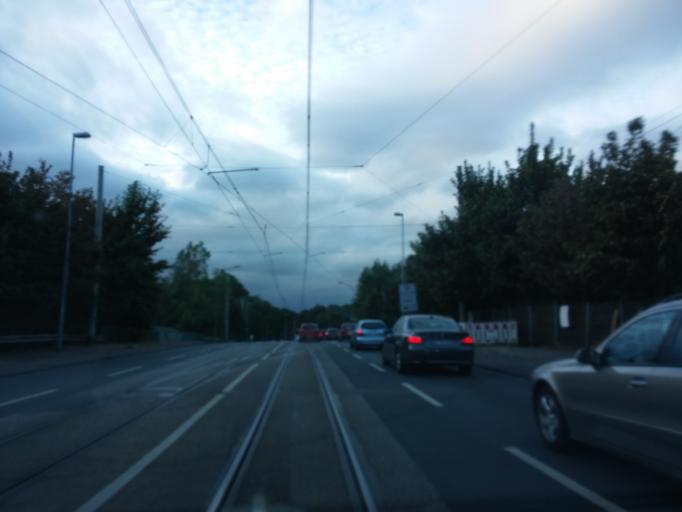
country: DE
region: North Rhine-Westphalia
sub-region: Regierungsbezirk Munster
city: Gladbeck
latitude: 51.5414
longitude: 7.0257
